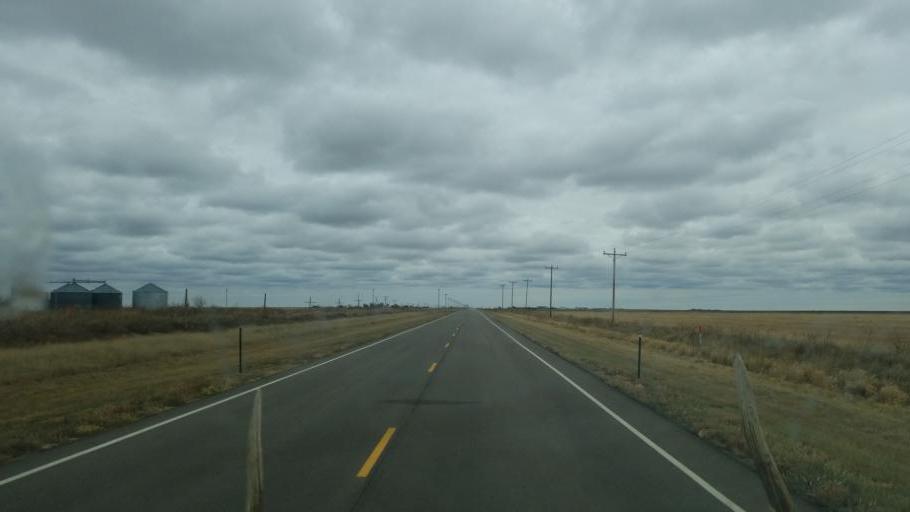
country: US
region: Colorado
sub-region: Kiowa County
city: Eads
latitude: 38.4866
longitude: -102.8629
